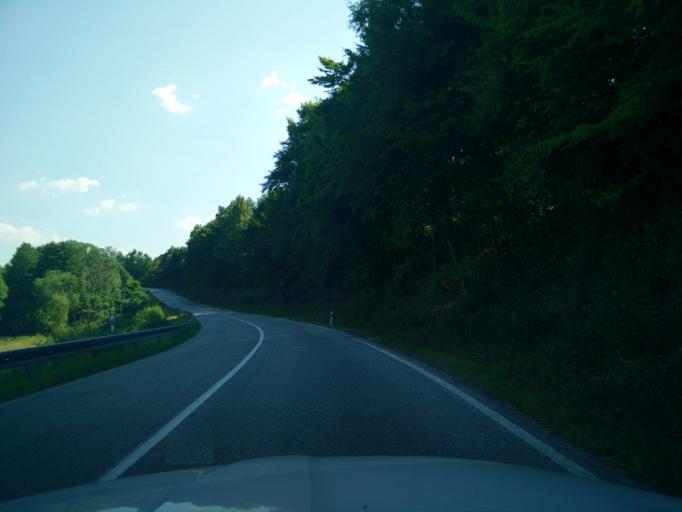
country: SK
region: Nitriansky
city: Bojnice
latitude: 48.8384
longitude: 18.4730
